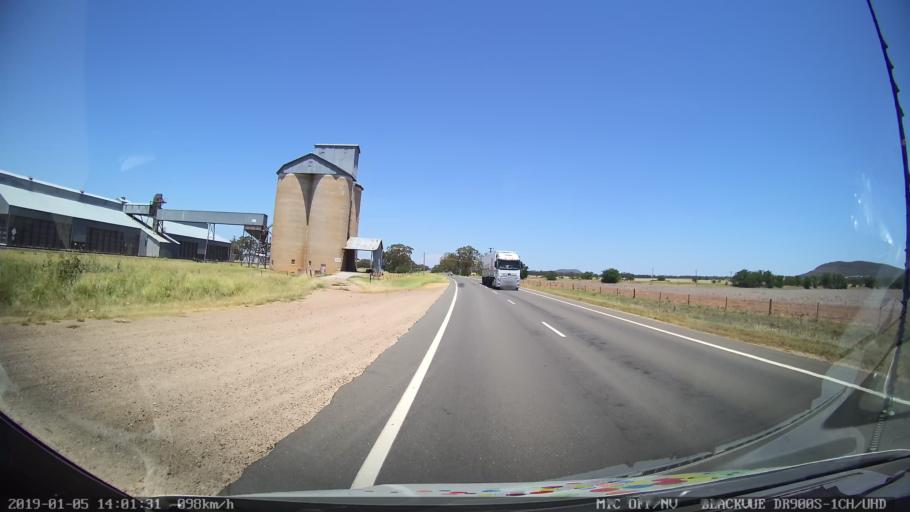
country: AU
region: New South Wales
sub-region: Gunnedah
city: Gunnedah
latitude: -31.1707
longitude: 150.3261
